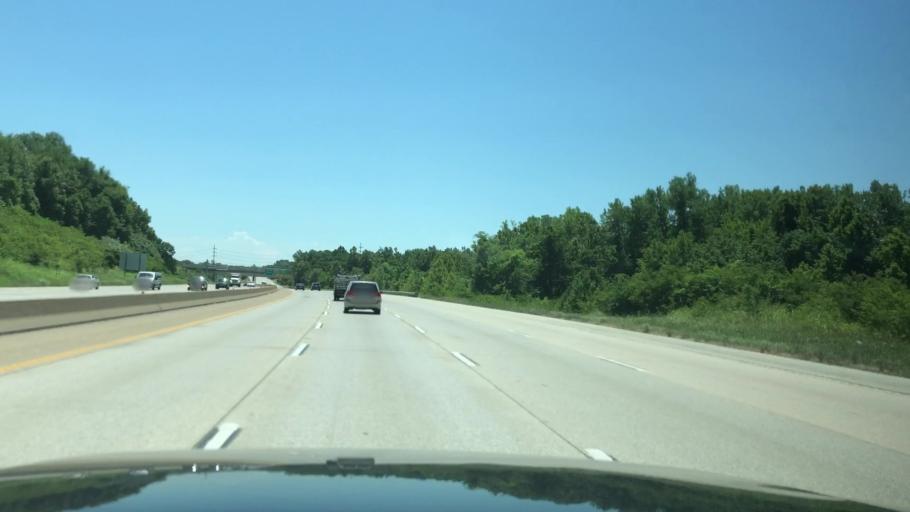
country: US
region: Missouri
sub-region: Saint Louis County
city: Bridgeton
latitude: 38.7790
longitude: -90.4157
